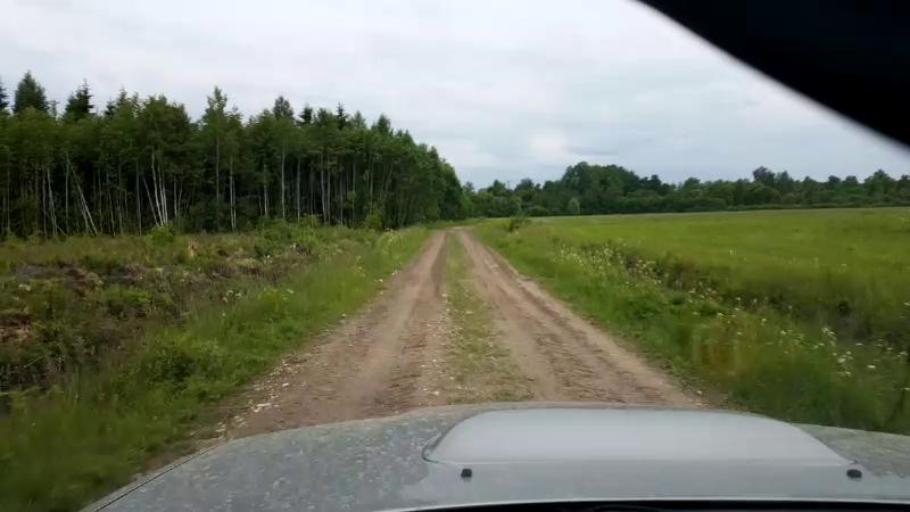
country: EE
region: Paernumaa
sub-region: Tootsi vald
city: Tootsi
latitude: 58.5972
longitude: 24.6628
